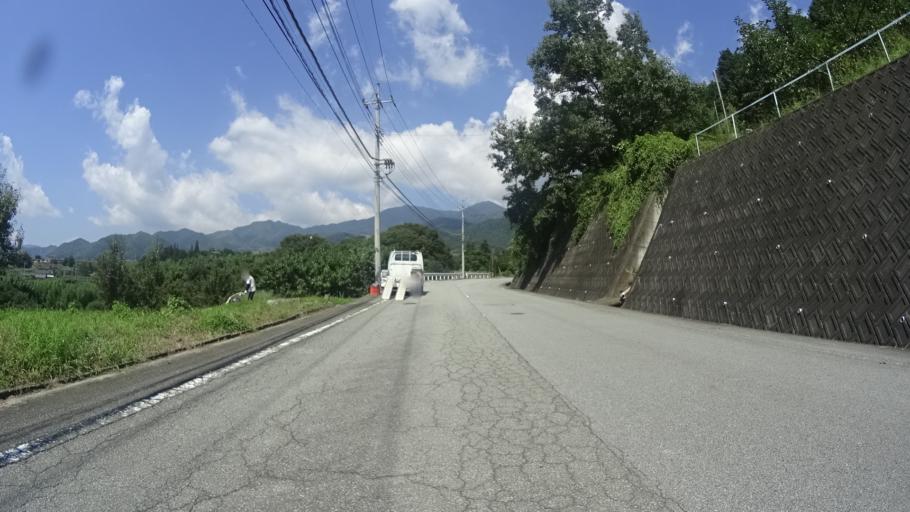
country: JP
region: Yamanashi
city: Enzan
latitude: 35.7532
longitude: 138.7123
